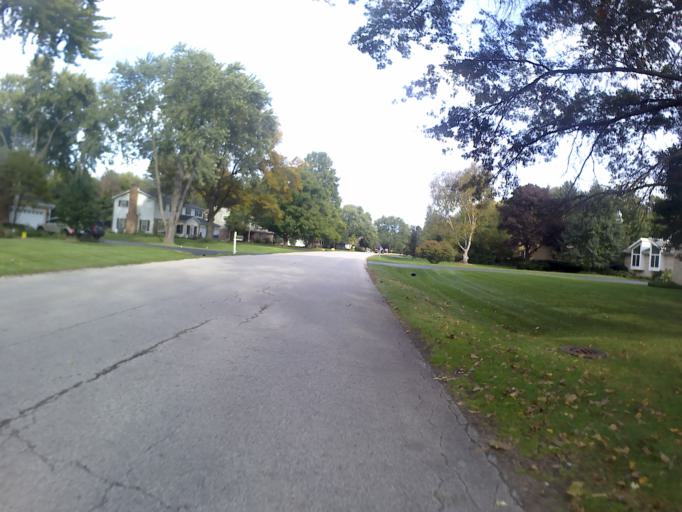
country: US
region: Illinois
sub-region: DuPage County
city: Winfield
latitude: 41.8396
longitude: -88.1348
